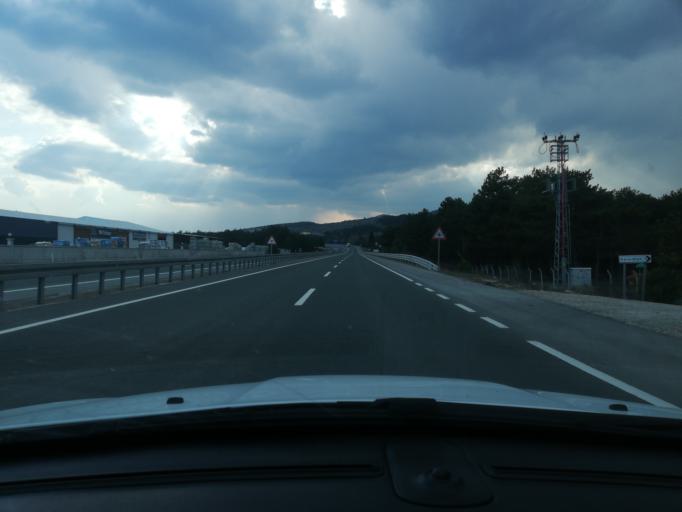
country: TR
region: Kastamonu
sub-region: Cide
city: Kastamonu
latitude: 41.3764
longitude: 33.7396
